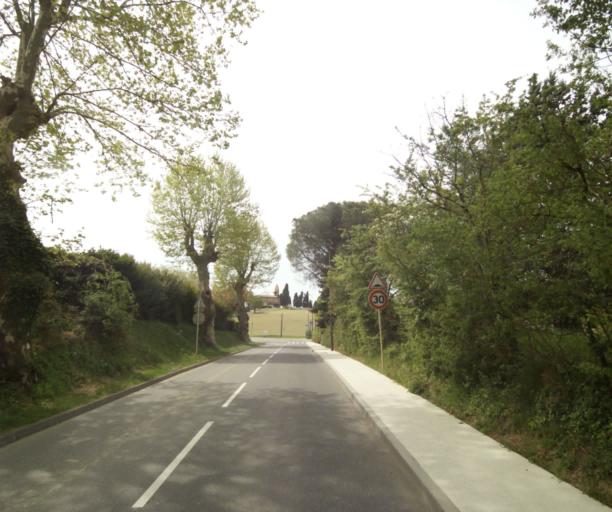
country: FR
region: Midi-Pyrenees
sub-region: Departement de la Haute-Garonne
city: Pompertuzat
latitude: 43.4903
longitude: 1.5142
